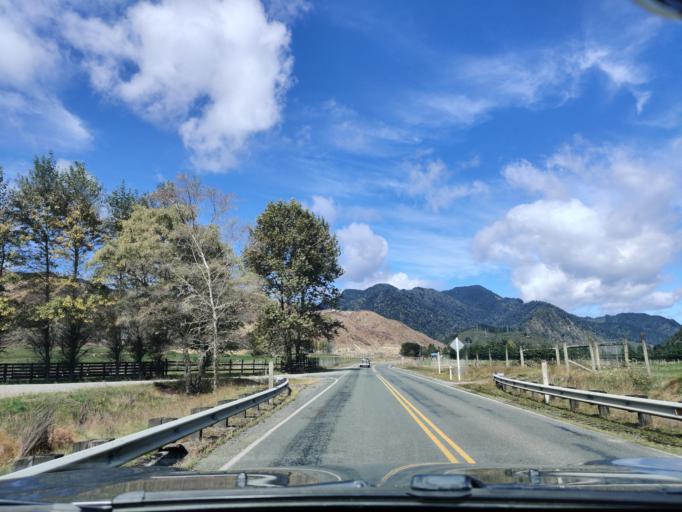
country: NZ
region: Tasman
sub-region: Tasman District
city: Wakefield
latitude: -41.7740
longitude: 172.3785
